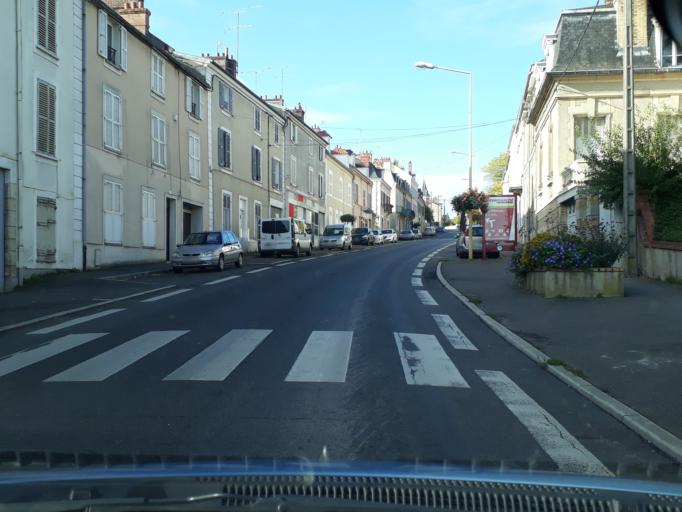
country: FR
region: Centre
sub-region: Departement du Loiret
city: Malesherbes
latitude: 48.2945
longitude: 2.4126
